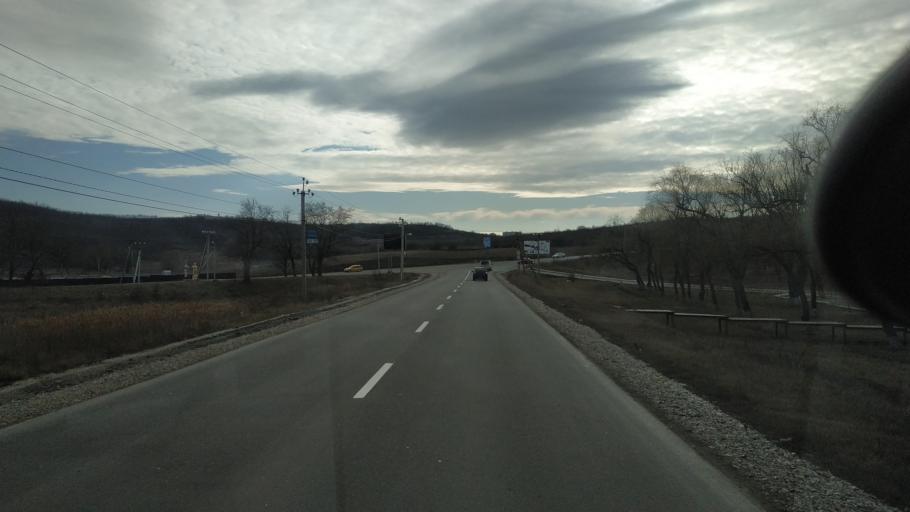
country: MD
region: Chisinau
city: Ciorescu
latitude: 47.0645
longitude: 28.9720
